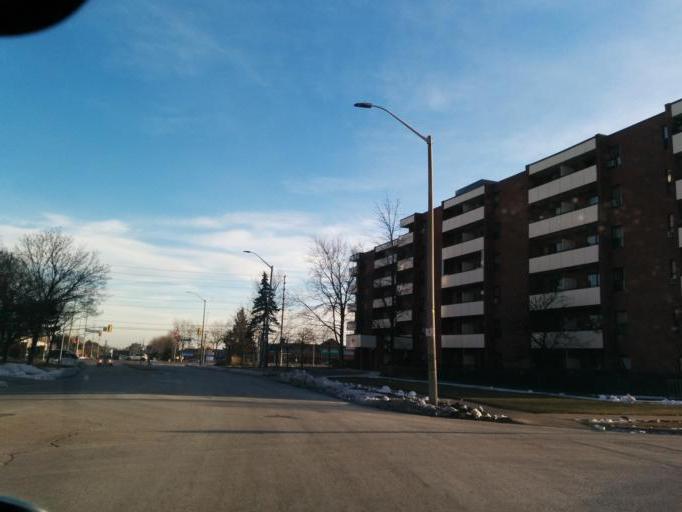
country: CA
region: Ontario
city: Etobicoke
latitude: 43.6077
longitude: -79.5877
